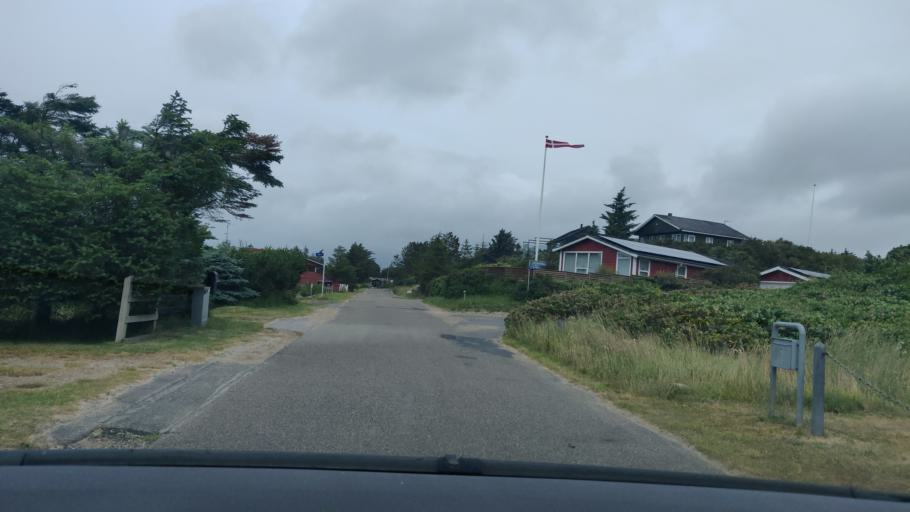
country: DK
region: North Denmark
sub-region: Jammerbugt Kommune
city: Pandrup
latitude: 57.2570
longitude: 9.5962
